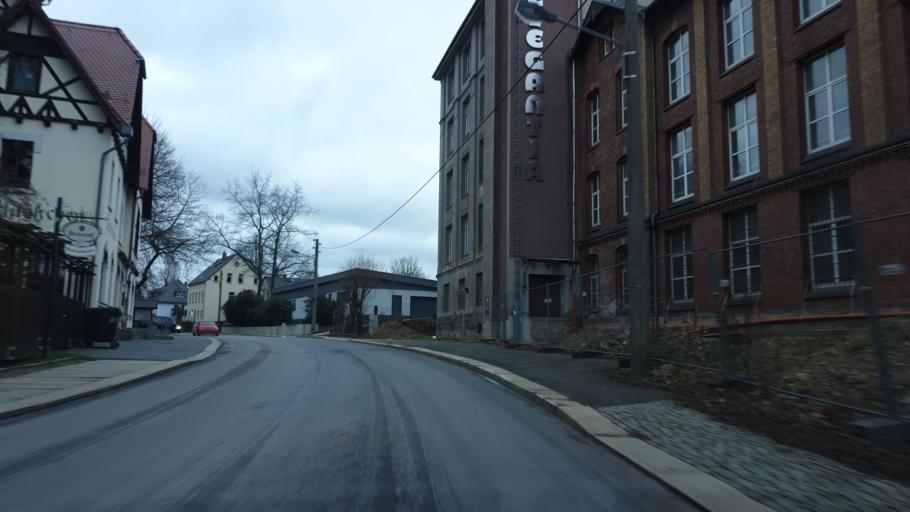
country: DE
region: Saxony
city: Lichtenstein
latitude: 50.7494
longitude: 12.6371
